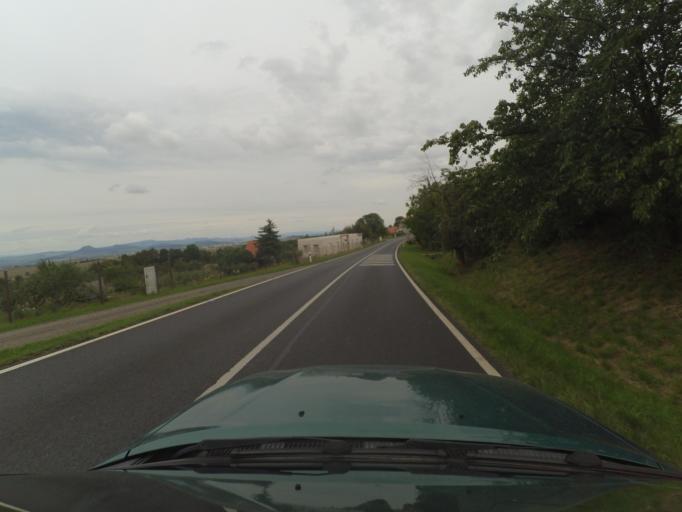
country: CZ
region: Ustecky
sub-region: Okres Louny
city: Louny
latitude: 50.3095
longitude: 13.7946
